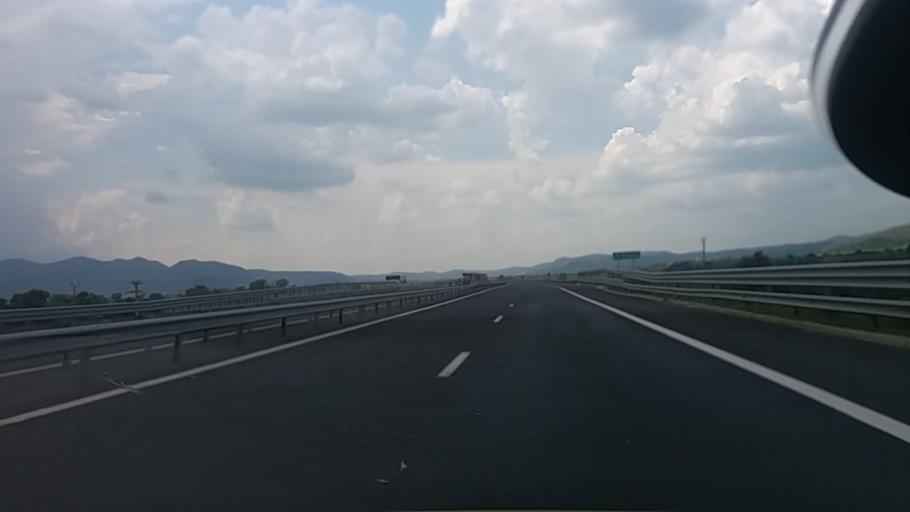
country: RO
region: Hunedoara
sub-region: Comuna Harau
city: Harau
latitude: 45.8845
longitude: 22.9855
